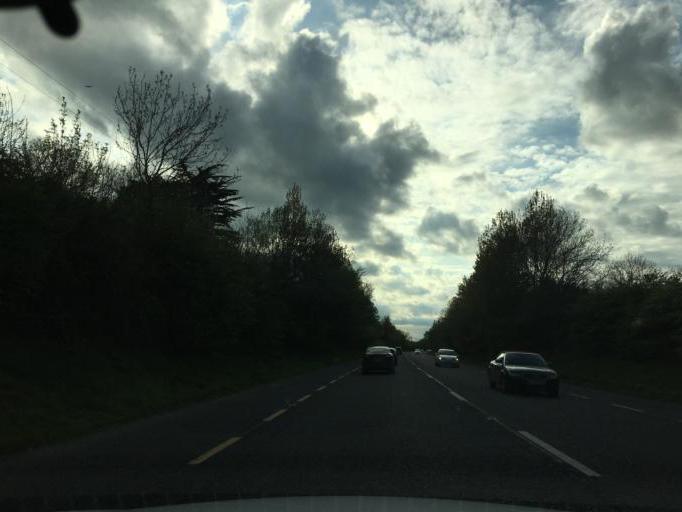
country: IE
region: Leinster
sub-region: Loch Garman
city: Loch Garman
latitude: 52.3384
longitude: -6.5511
